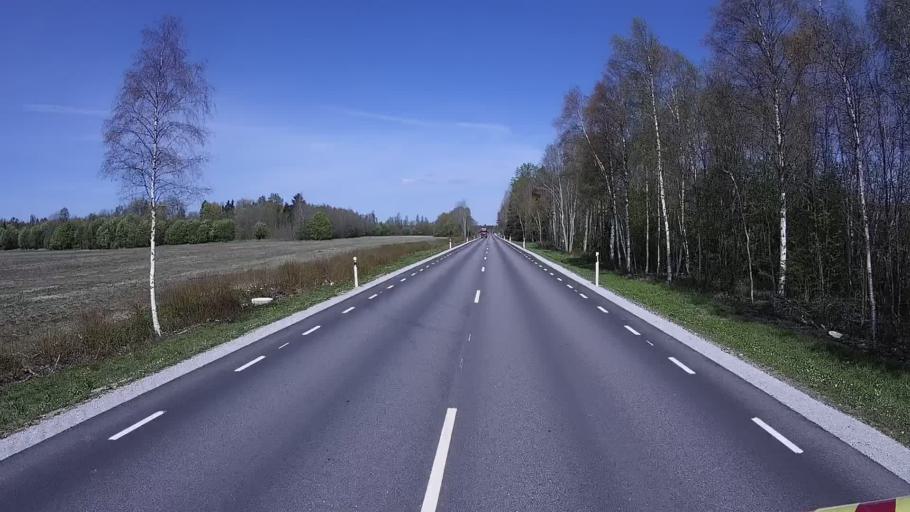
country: EE
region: Harju
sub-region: Nissi vald
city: Turba
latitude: 59.1637
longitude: 24.0742
